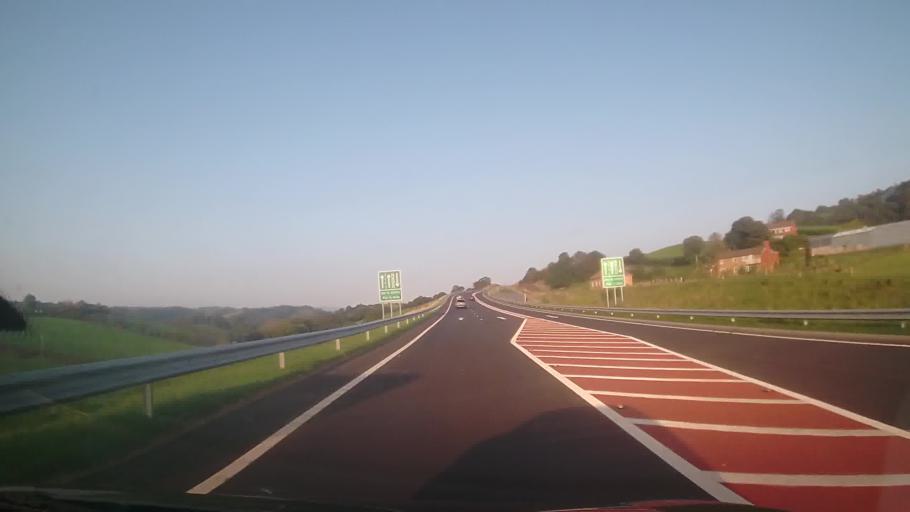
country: GB
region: Wales
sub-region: Sir Powys
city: Newtown
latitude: 52.5087
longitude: -3.3078
